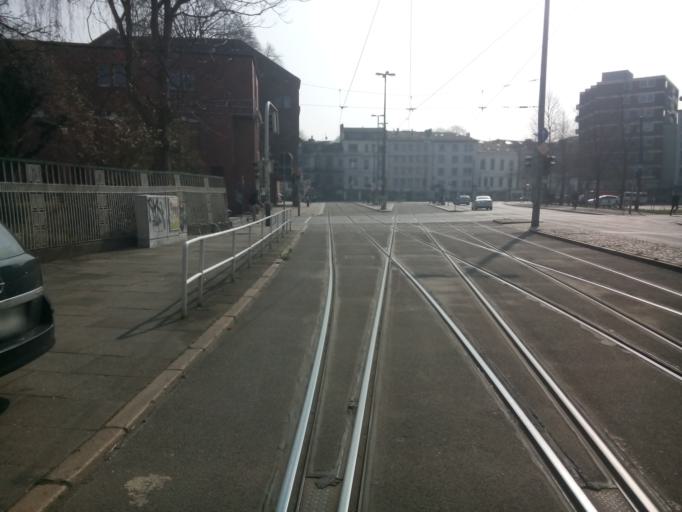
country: DE
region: Bremen
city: Bremen
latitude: 53.0787
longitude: 8.8225
